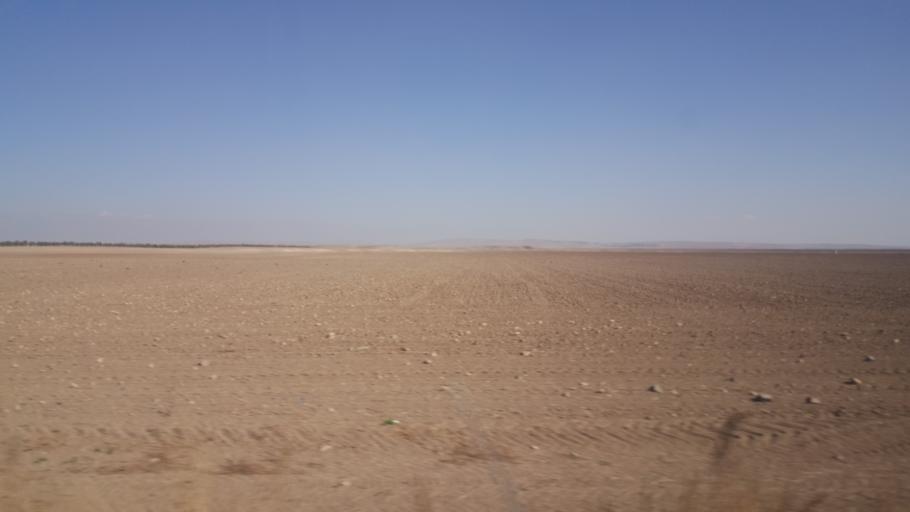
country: TR
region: Konya
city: Suluklu
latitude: 39.0034
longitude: 32.1095
